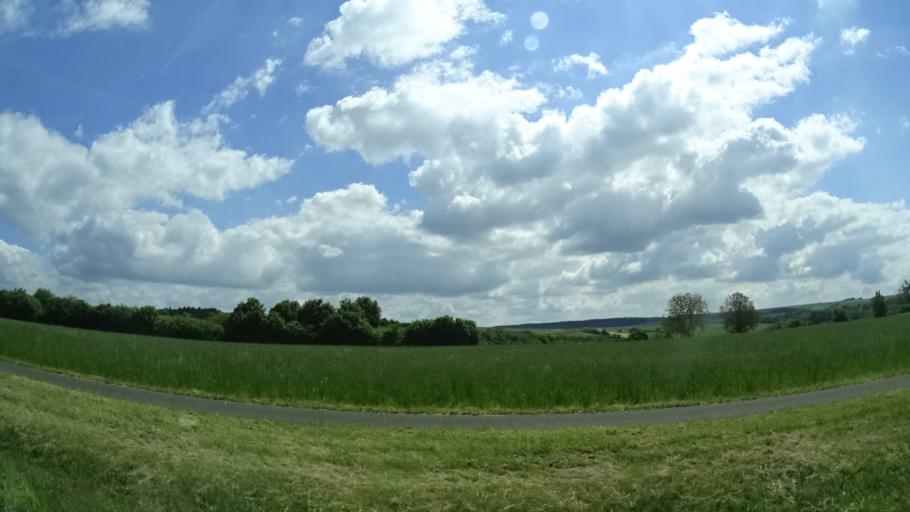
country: DE
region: Bavaria
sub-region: Regierungsbezirk Unterfranken
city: Mellrichstadt
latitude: 50.4395
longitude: 10.3084
